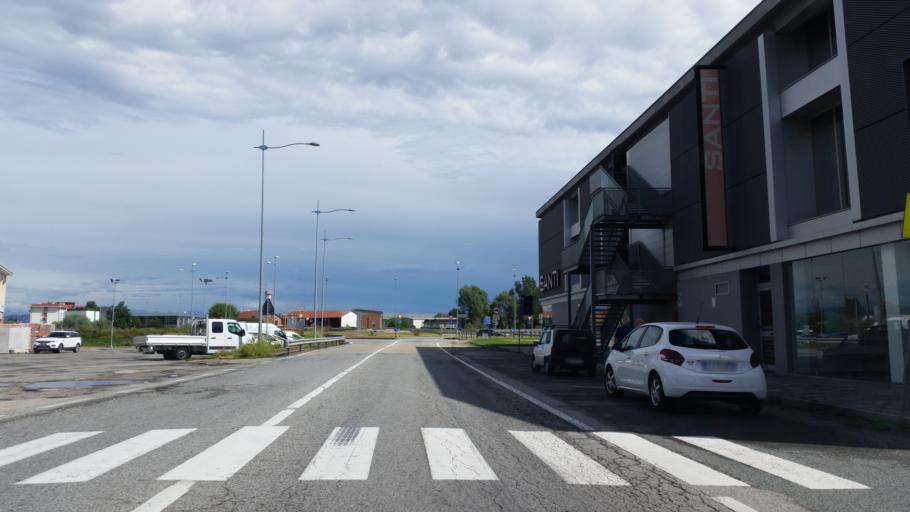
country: IT
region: Piedmont
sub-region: Provincia di Torino
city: Poirino
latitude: 44.9232
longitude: 7.8380
